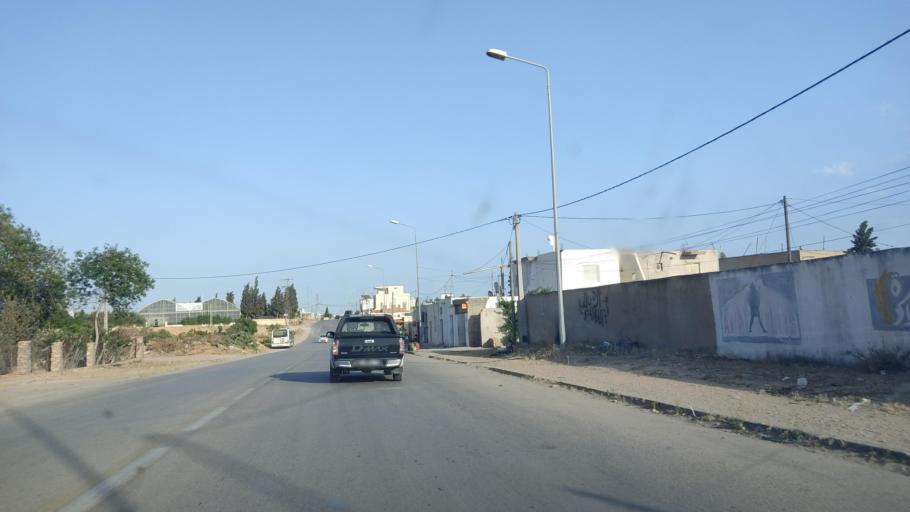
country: TN
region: Safaqis
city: Sfax
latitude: 34.7955
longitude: 10.6811
